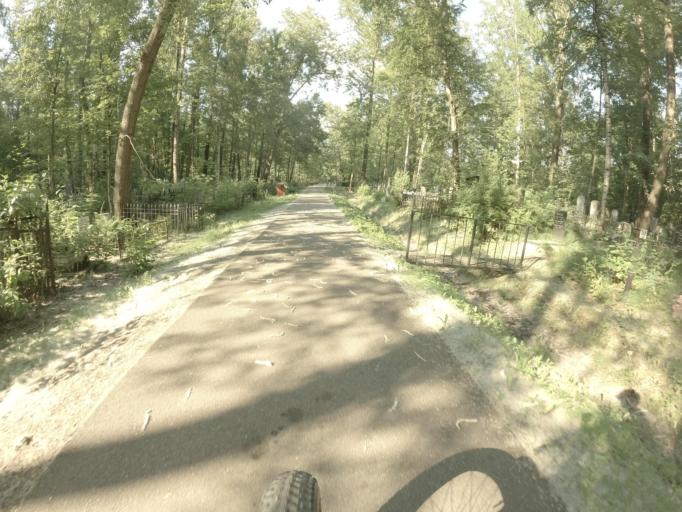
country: RU
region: St.-Petersburg
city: Obukhovo
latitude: 59.8550
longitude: 30.4522
